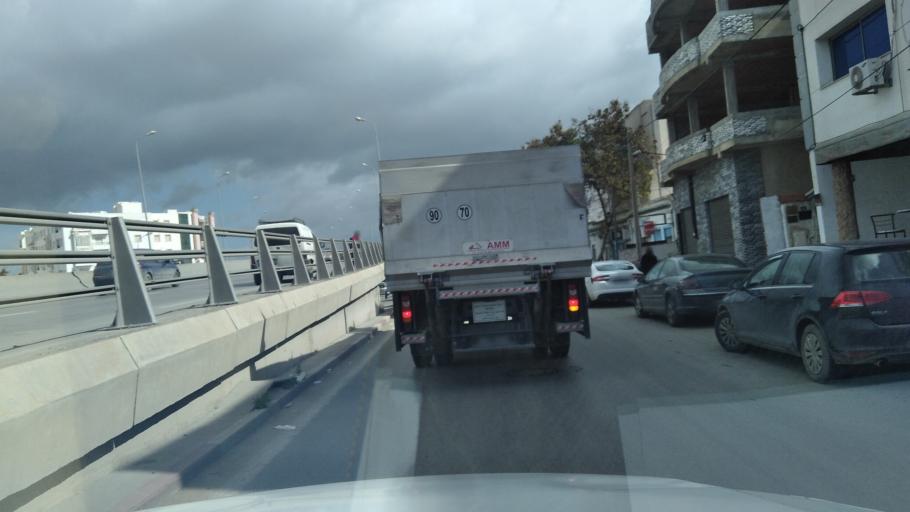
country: TN
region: Bin 'Arus
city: Ben Arous
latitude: 36.7544
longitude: 10.2462
